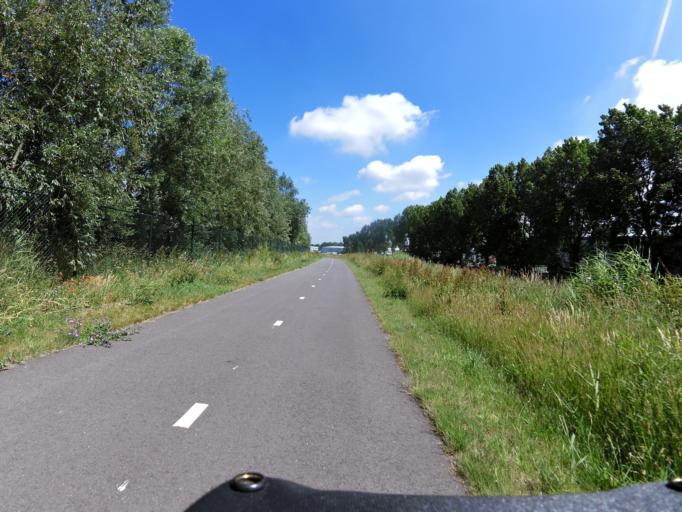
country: NL
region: South Holland
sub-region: Gemeente Schiedam
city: Schiedam
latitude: 51.9465
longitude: 4.3975
